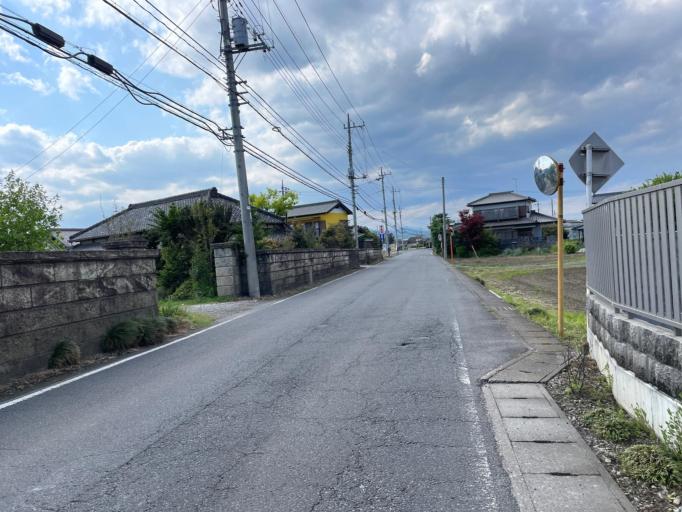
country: JP
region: Tochigi
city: Tochigi
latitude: 36.4112
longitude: 139.7346
